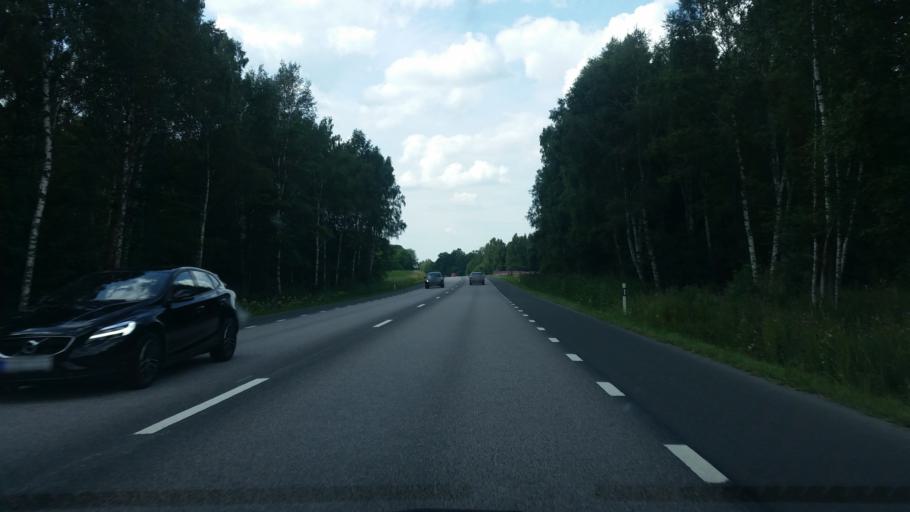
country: SE
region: Vaestra Goetaland
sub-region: Skara Kommun
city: Axvall
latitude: 58.3919
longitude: 13.6420
